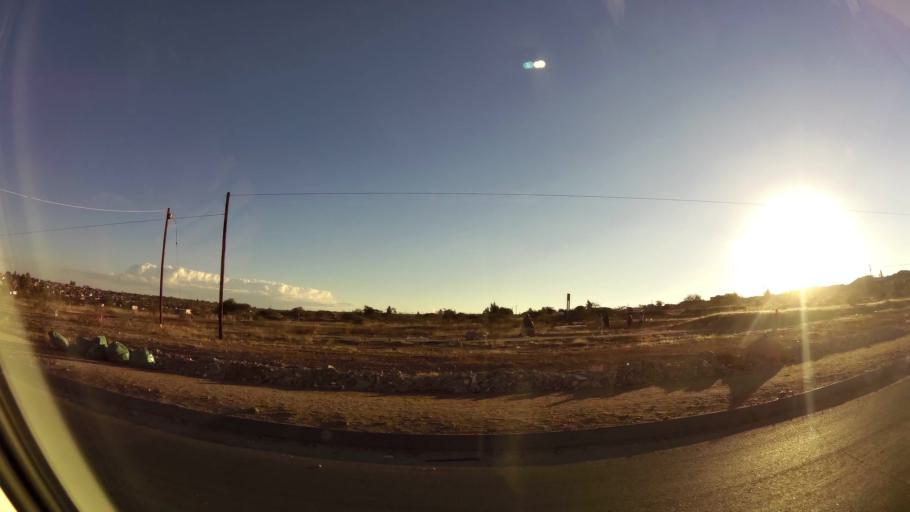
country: ZA
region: Limpopo
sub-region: Capricorn District Municipality
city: Polokwane
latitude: -23.8400
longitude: 29.3521
